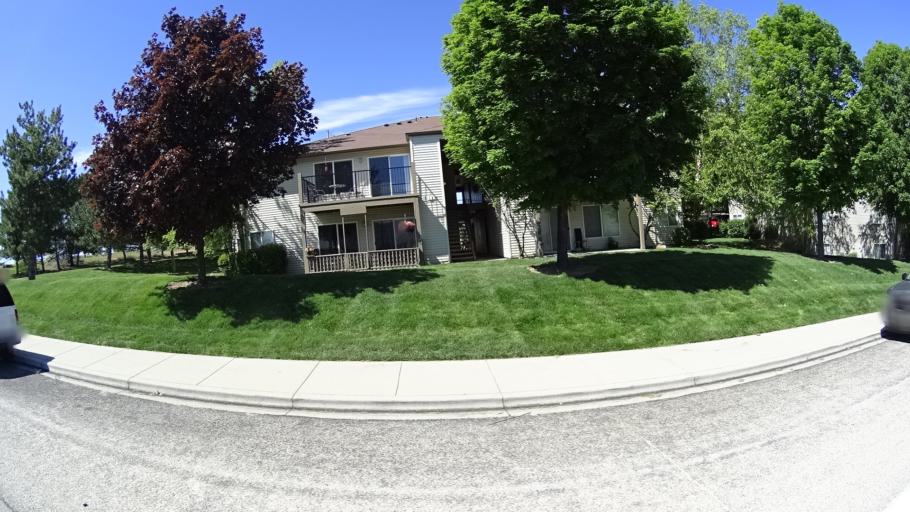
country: US
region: Idaho
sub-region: Ada County
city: Boise
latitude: 43.5421
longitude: -116.1491
